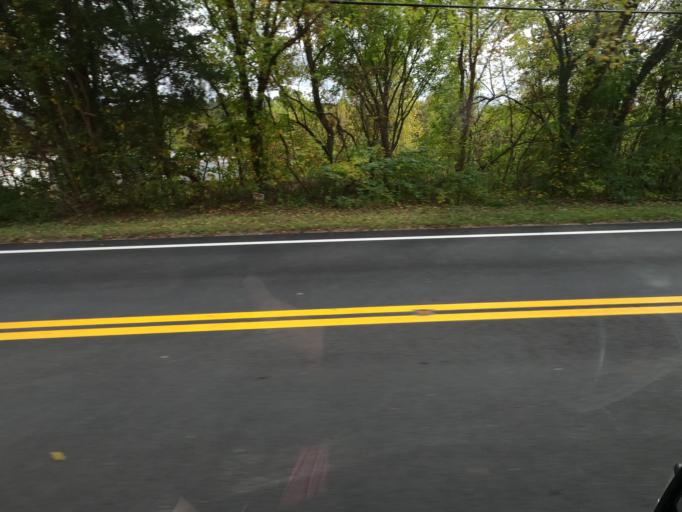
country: US
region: Tennessee
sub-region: Carter County
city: Pine Crest
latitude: 36.3259
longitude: -82.3176
